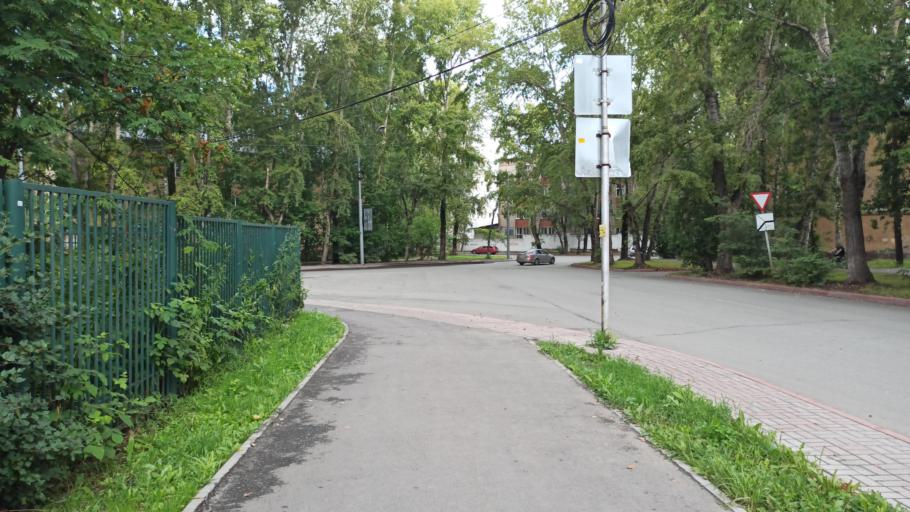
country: RU
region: Tomsk
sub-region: Tomskiy Rayon
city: Tomsk
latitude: 56.4630
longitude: 84.9822
